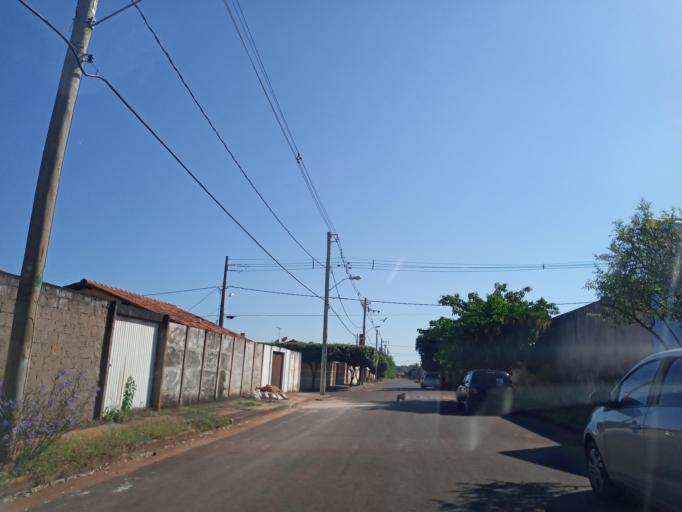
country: BR
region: Minas Gerais
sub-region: Ituiutaba
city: Ituiutaba
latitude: -18.9747
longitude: -49.4890
